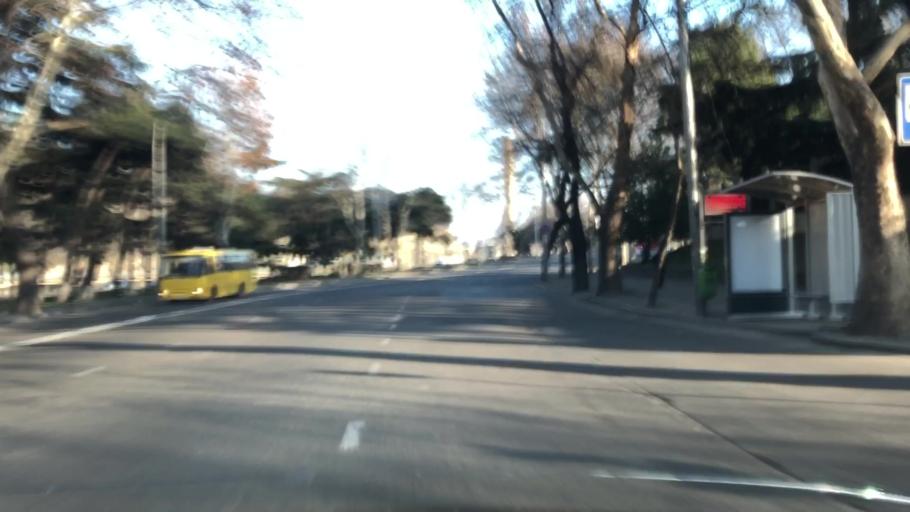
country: GE
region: T'bilisi
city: Tbilisi
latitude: 41.6880
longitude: 44.8184
